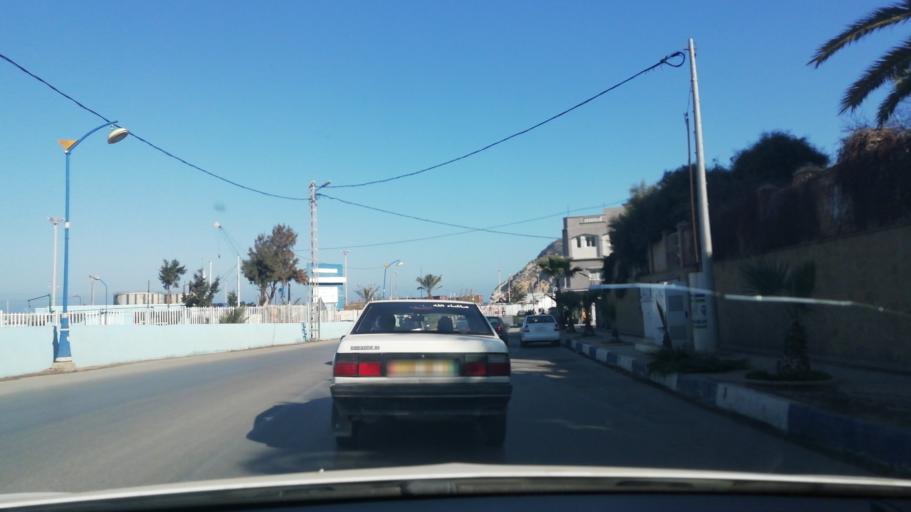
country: DZ
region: Tlemcen
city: Nedroma
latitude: 35.0985
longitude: -1.8636
